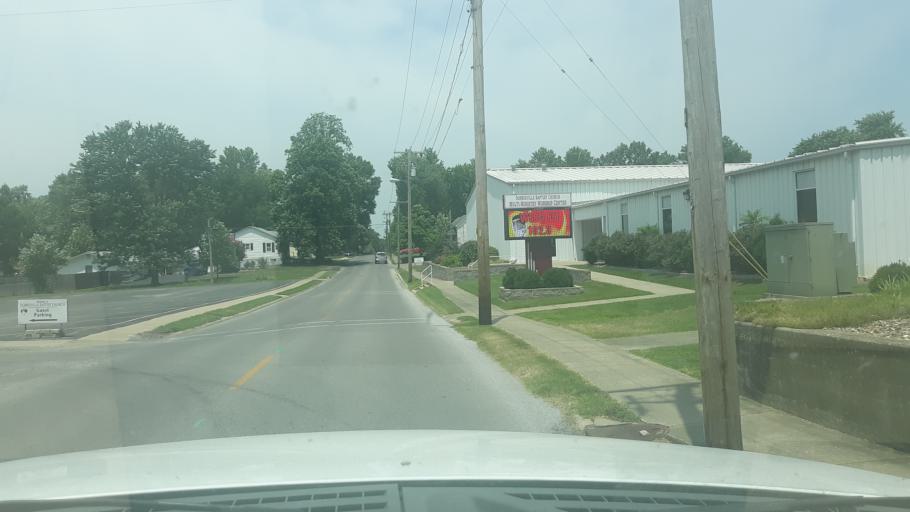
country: US
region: Illinois
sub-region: Saline County
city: Harrisburg
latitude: 37.7226
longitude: -88.5531
